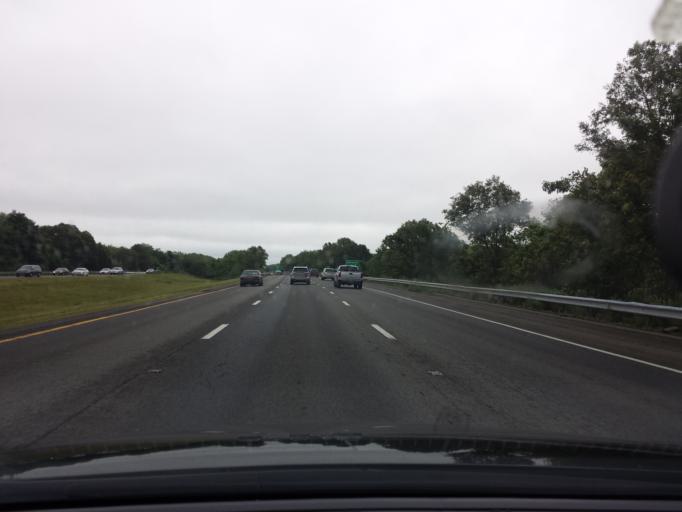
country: US
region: Rhode Island
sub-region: Bristol County
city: Barrington
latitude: 41.7793
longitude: -71.2816
